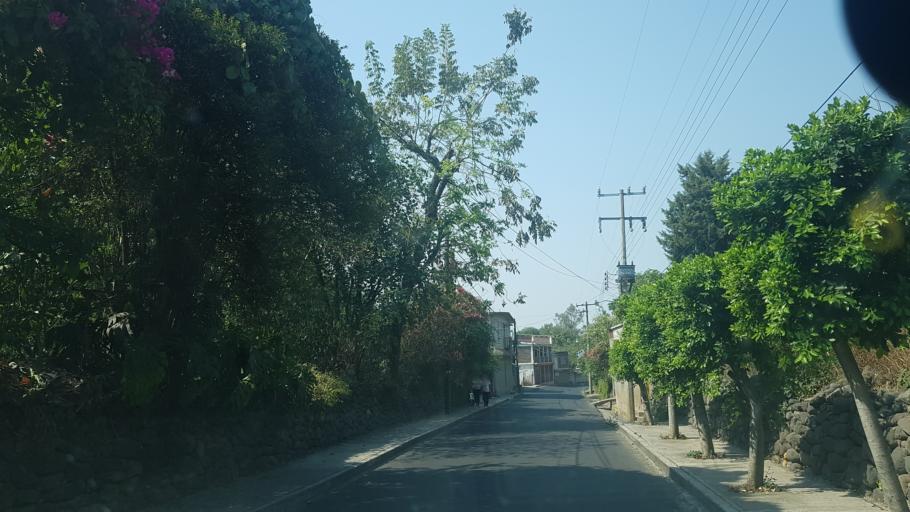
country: MX
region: Morelos
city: Tlacotepec
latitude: 18.8120
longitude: -98.7542
